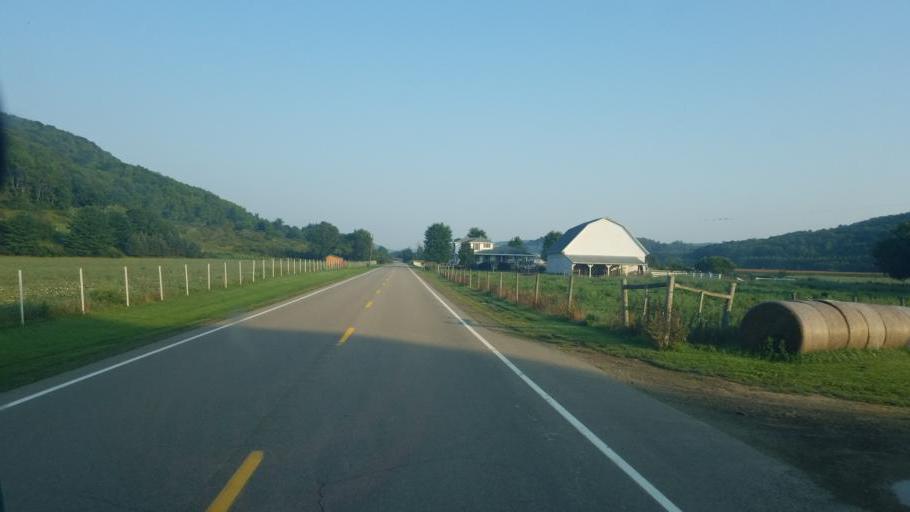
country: US
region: Pennsylvania
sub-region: Tioga County
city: Westfield
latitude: 41.9732
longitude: -77.4599
